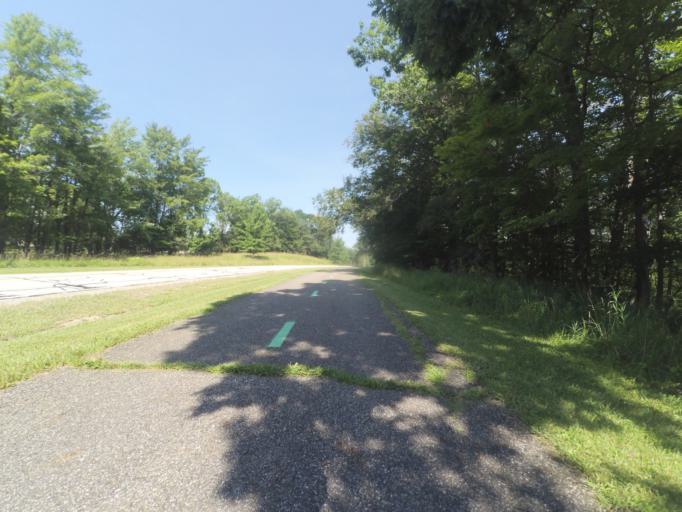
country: US
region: Ohio
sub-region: Cuyahoga County
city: Oakwood
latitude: 41.3767
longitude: -81.4940
